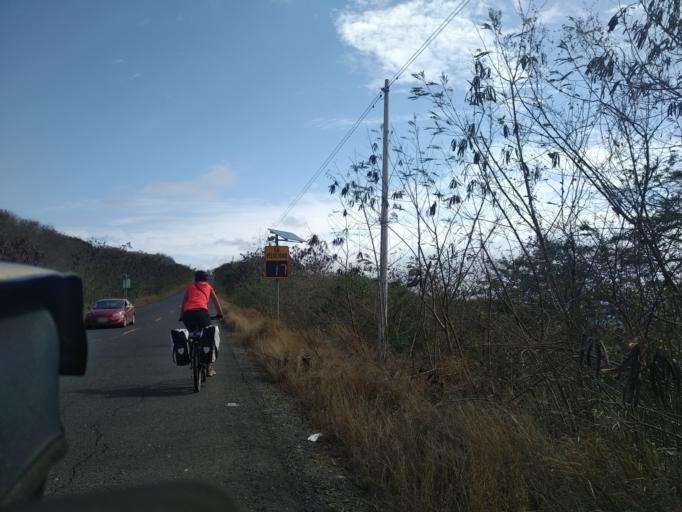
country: EC
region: Manabi
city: Jipijapa
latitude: -1.4579
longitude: -80.7611
